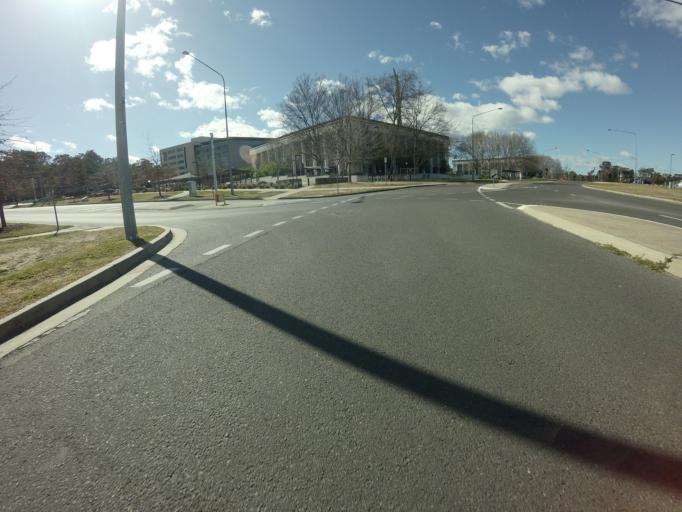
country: AU
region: Australian Capital Territory
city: Canberra
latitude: -35.2966
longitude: 149.1497
